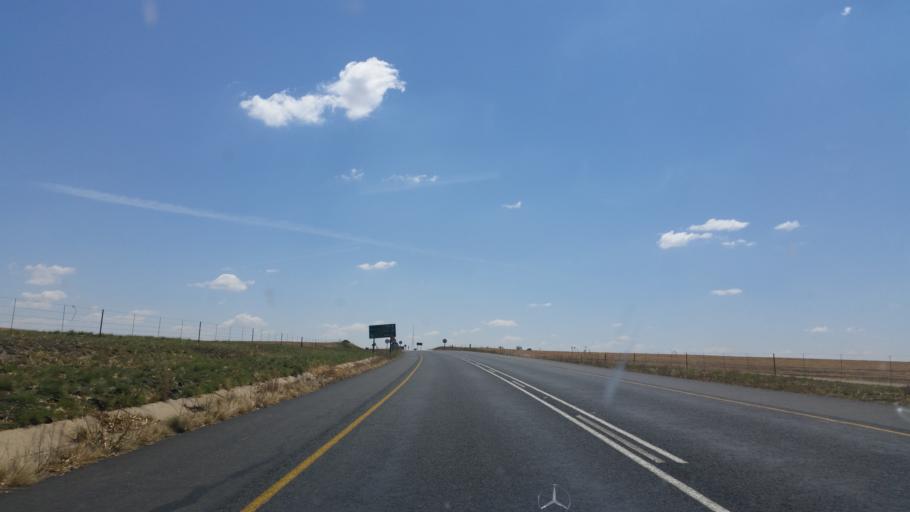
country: ZA
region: Orange Free State
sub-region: Thabo Mofutsanyana District Municipality
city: Reitz
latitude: -28.0861
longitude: 28.6517
